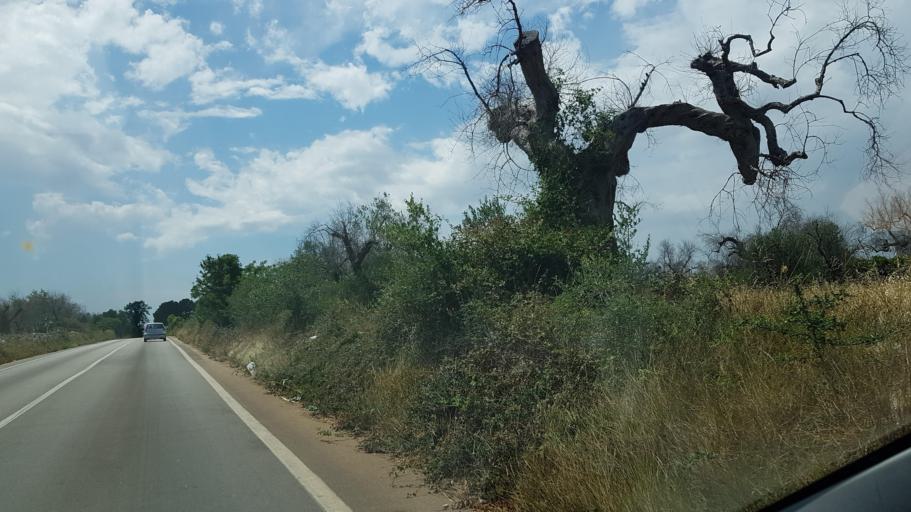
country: IT
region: Apulia
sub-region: Provincia di Lecce
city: Ruffano
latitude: 39.9603
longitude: 18.2436
